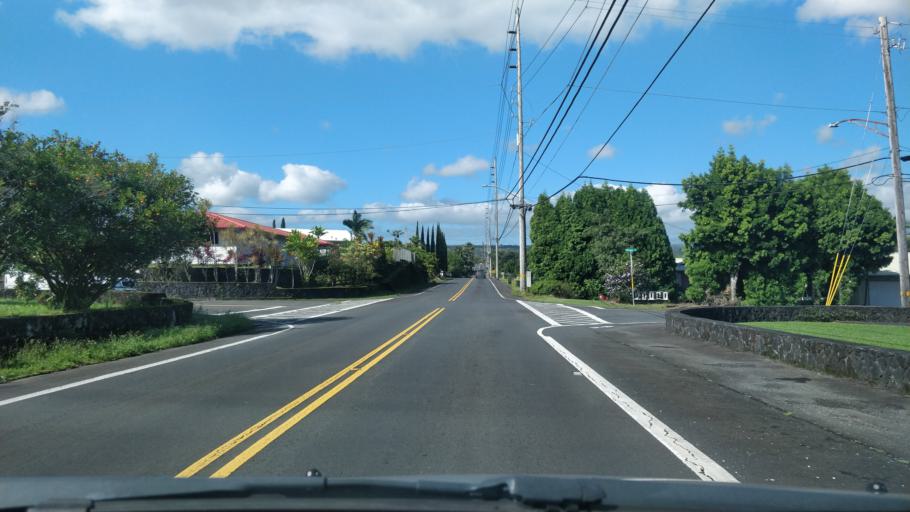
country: US
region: Hawaii
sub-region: Hawaii County
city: Hilo
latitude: 19.6825
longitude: -155.0983
